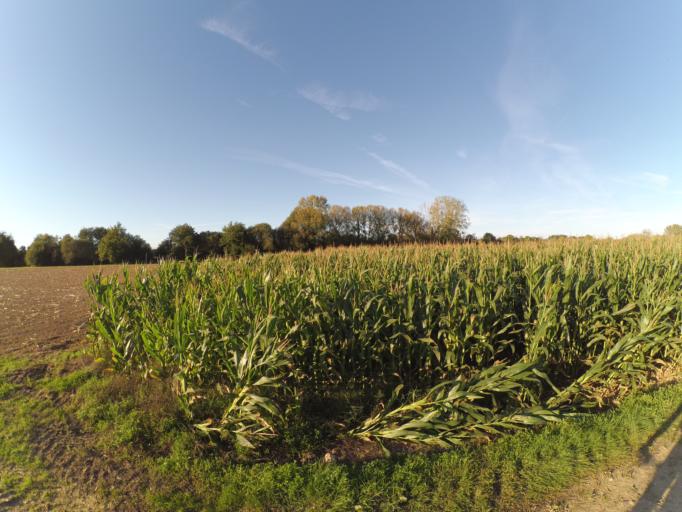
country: FR
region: Brittany
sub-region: Departement du Morbihan
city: Saint-Vincent-sur-Oust
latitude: 47.7236
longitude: -2.1795
